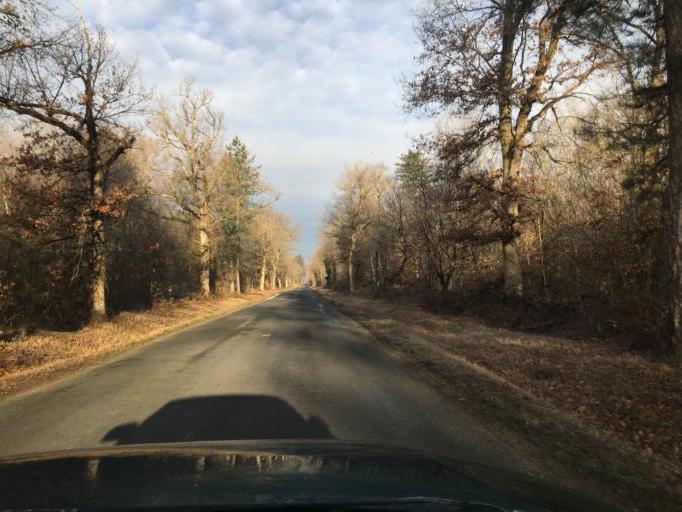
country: FR
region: Centre
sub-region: Departement du Loiret
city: Jouy-le-Potier
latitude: 47.8025
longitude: 1.8203
